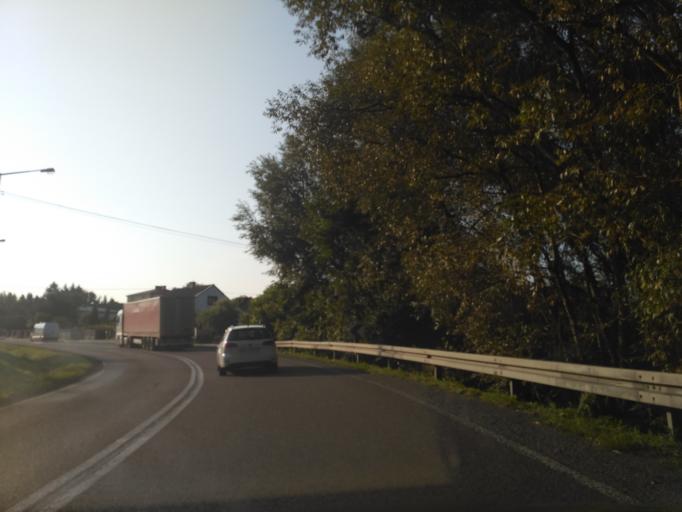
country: PL
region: Lublin Voivodeship
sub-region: Powiat janowski
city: Modliborzyce
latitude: 50.7576
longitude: 22.3219
